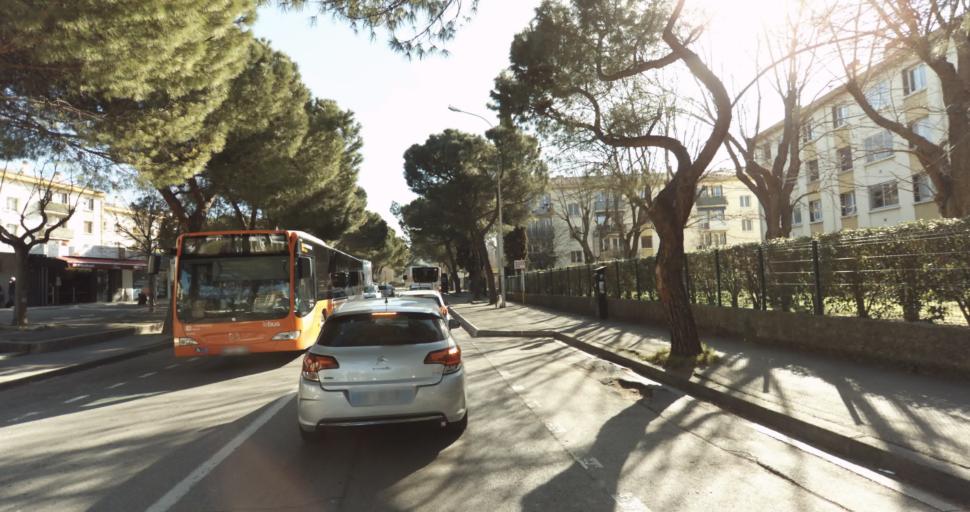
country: FR
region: Provence-Alpes-Cote d'Azur
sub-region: Departement des Bouches-du-Rhone
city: Aix-en-Provence
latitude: 43.5141
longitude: 5.4619
